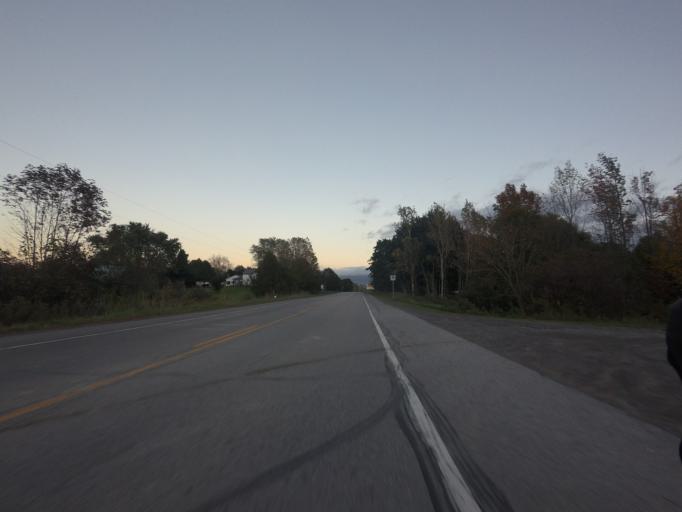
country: CA
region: Ontario
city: Quinte West
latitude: 44.0410
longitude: -77.6714
